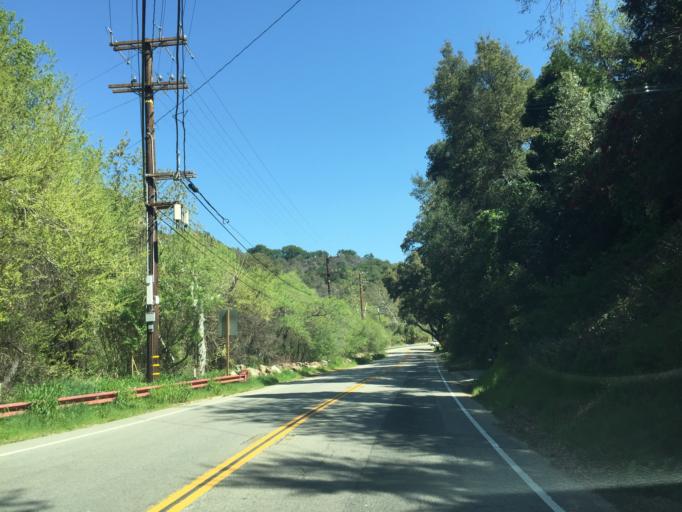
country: US
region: California
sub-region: Los Angeles County
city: Topanga
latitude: 34.1003
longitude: -118.5979
